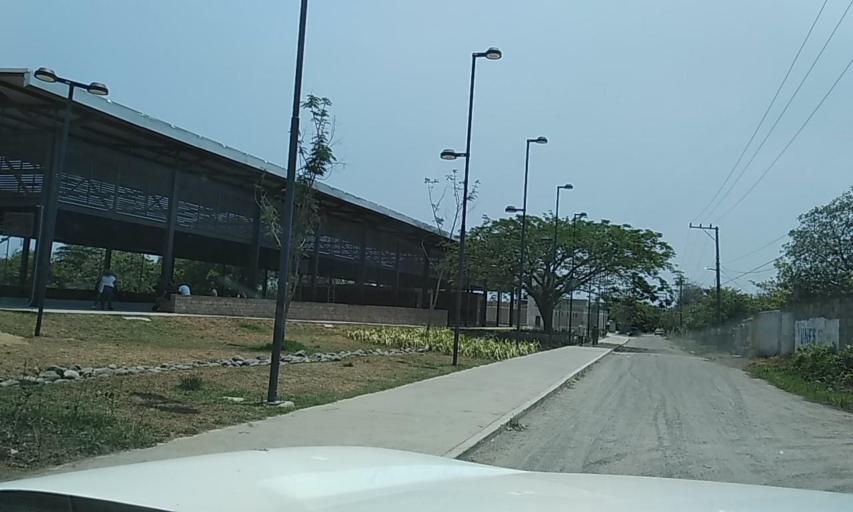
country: MX
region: Veracruz
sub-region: Veracruz
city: Las Amapolas
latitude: 19.1408
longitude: -96.1986
